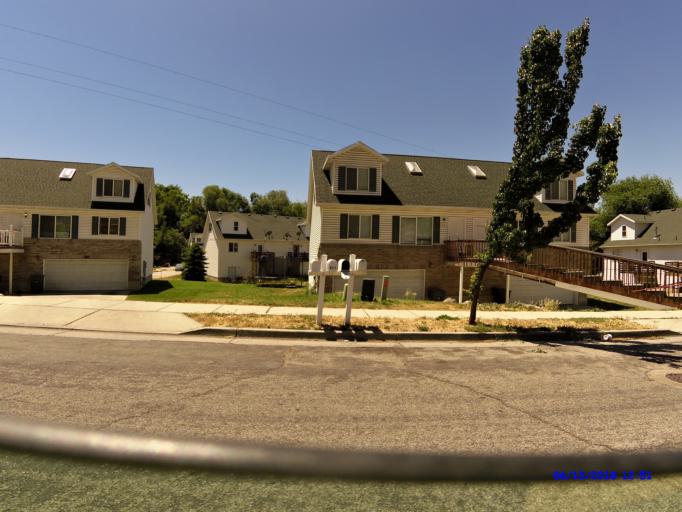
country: US
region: Utah
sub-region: Weber County
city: South Ogden
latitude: 41.2081
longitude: -111.9576
